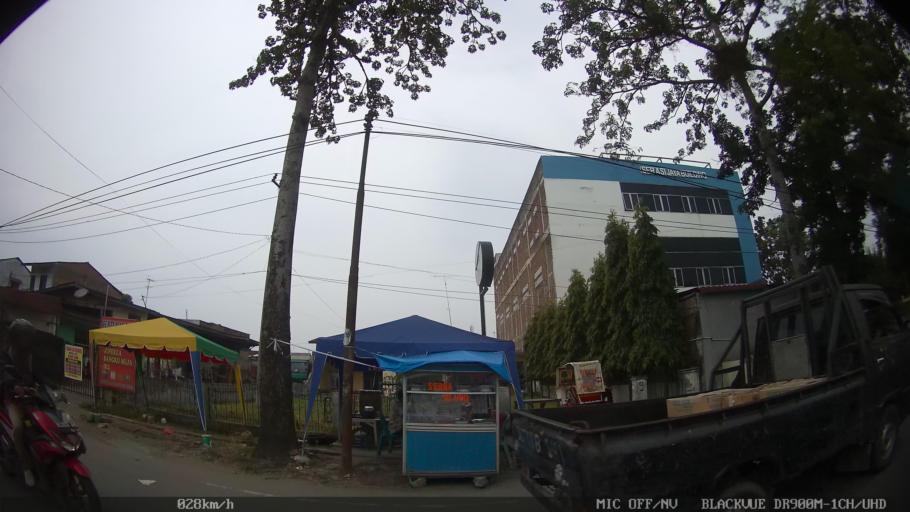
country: ID
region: North Sumatra
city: Medan
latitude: 3.5611
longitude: 98.7031
